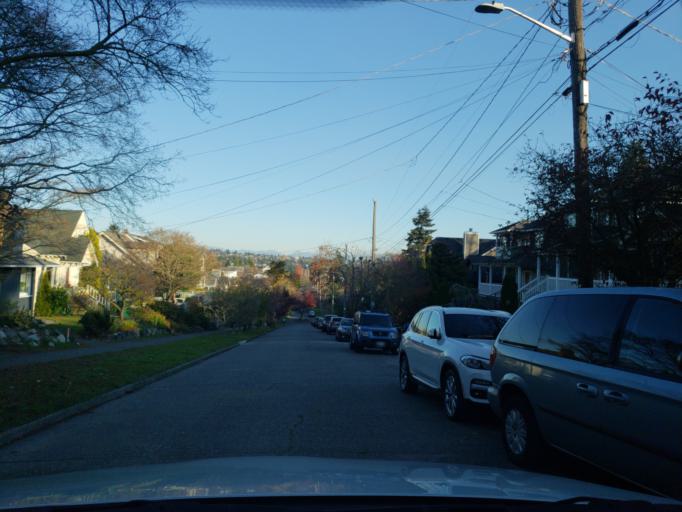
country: US
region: Washington
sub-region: King County
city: Shoreline
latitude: 47.6848
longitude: -122.3545
